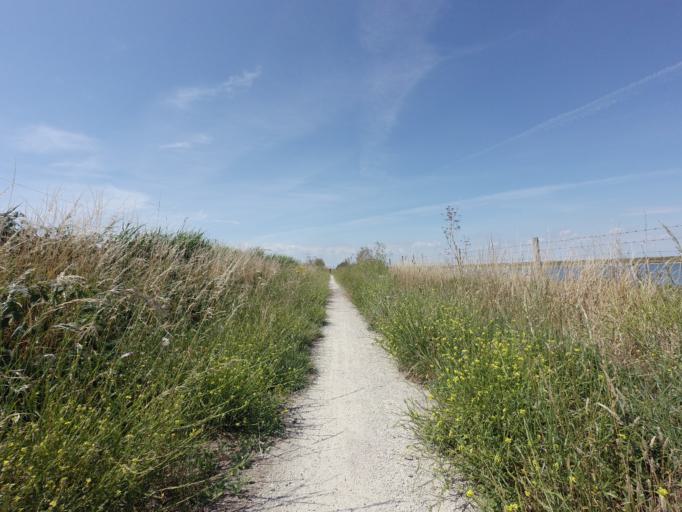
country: GB
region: England
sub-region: Kent
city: Lydd
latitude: 50.9345
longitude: 0.8553
